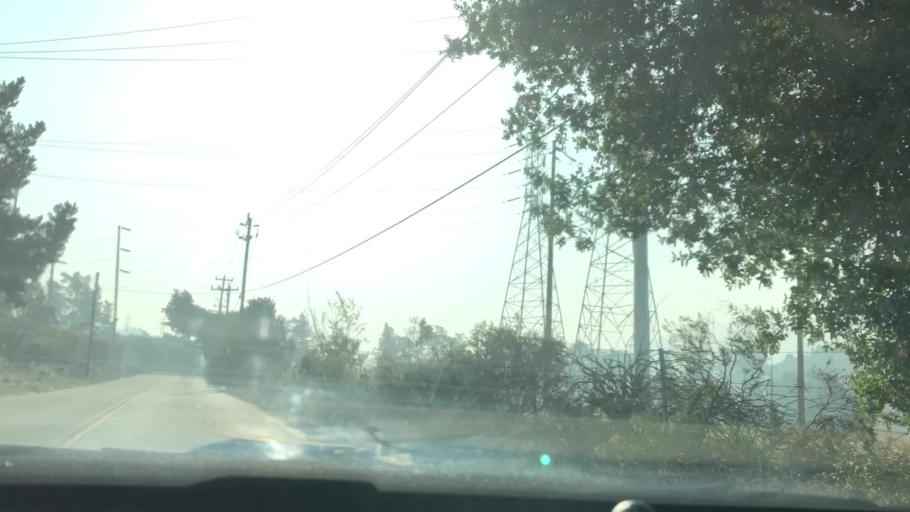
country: US
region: California
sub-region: Contra Costa County
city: Orinda
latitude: 37.9052
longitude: -122.2098
